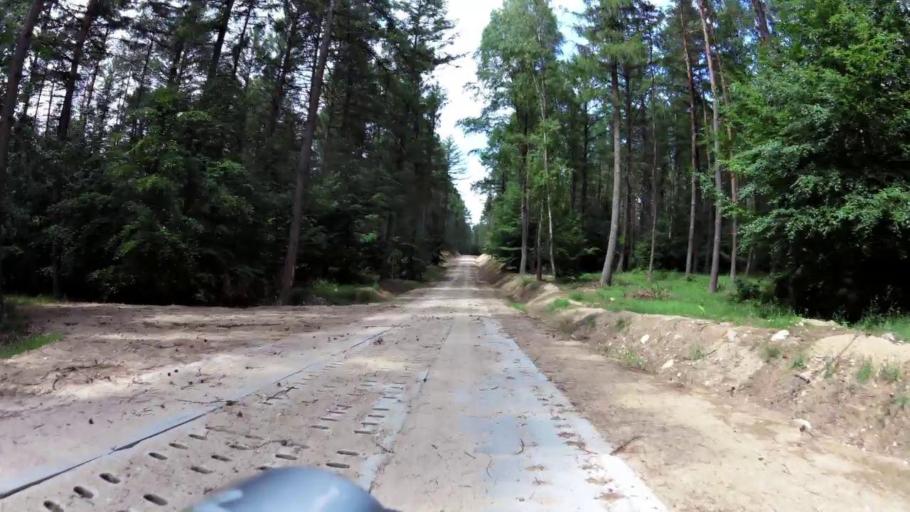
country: PL
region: West Pomeranian Voivodeship
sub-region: Powiat szczecinecki
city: Bialy Bor
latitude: 53.9573
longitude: 16.7562
